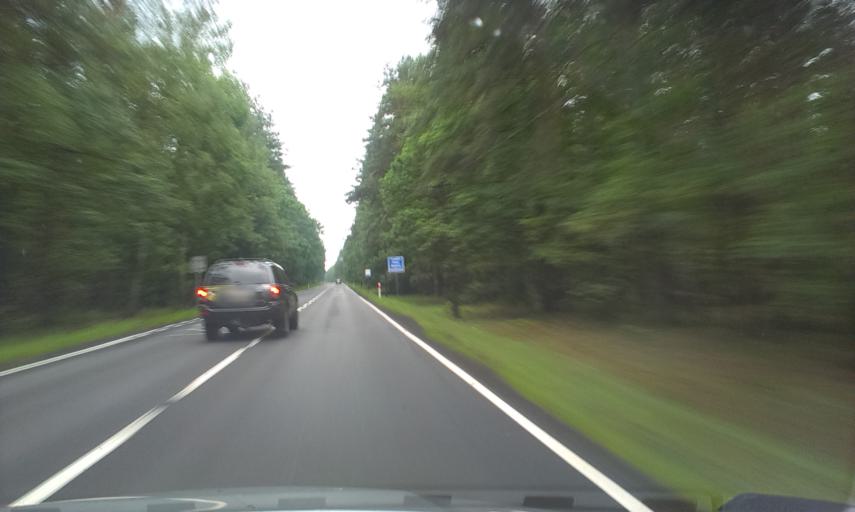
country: PL
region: Greater Poland Voivodeship
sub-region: Powiat zlotowski
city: Tarnowka
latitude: 53.2912
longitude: 16.7821
